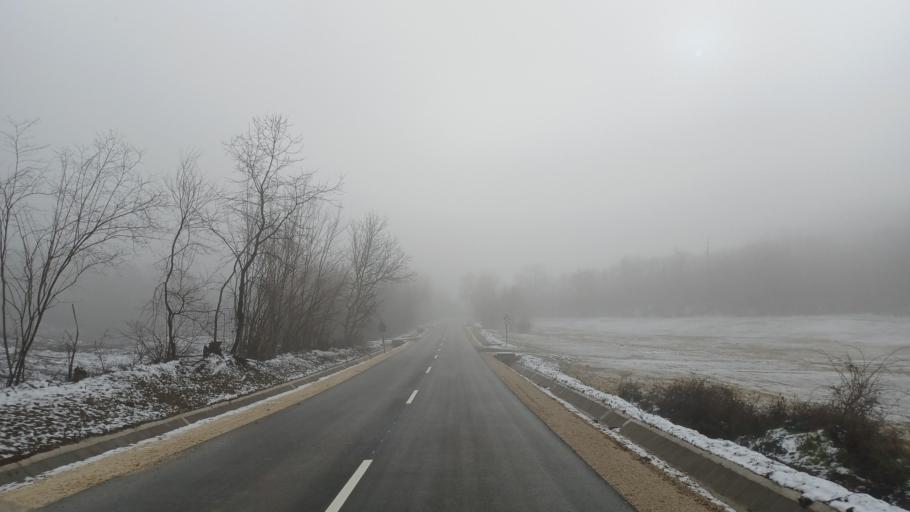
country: HU
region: Tolna
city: Gyonk
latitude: 46.5830
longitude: 18.4743
